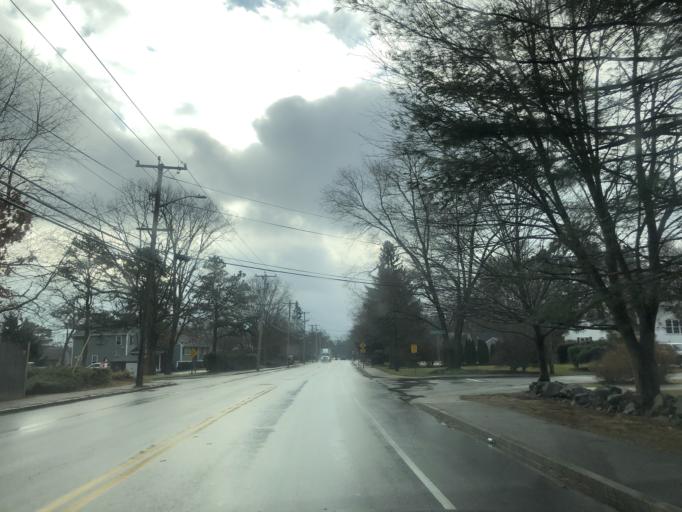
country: US
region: Massachusetts
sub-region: Norfolk County
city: Plainville
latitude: 42.0034
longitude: -71.2973
